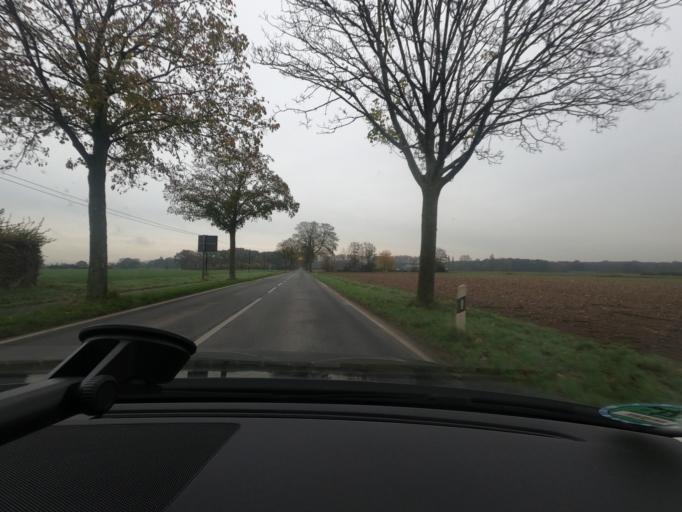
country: DE
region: North Rhine-Westphalia
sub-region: Regierungsbezirk Dusseldorf
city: Kevelaer
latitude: 51.6068
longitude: 6.2847
